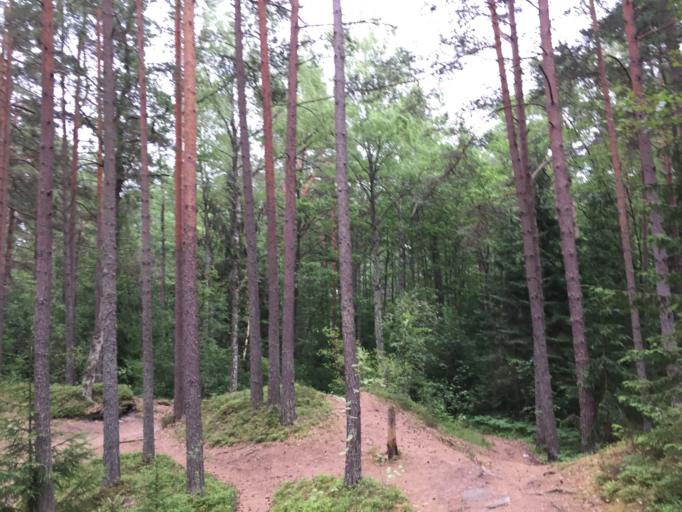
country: LV
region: Carnikava
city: Carnikava
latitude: 57.1203
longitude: 24.2201
